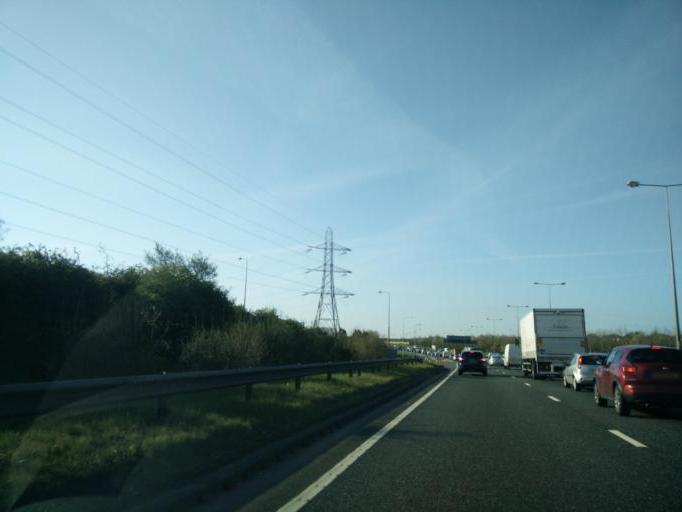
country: GB
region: England
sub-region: Stockton-on-Tees
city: Billingham
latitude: 54.5900
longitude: -1.3013
